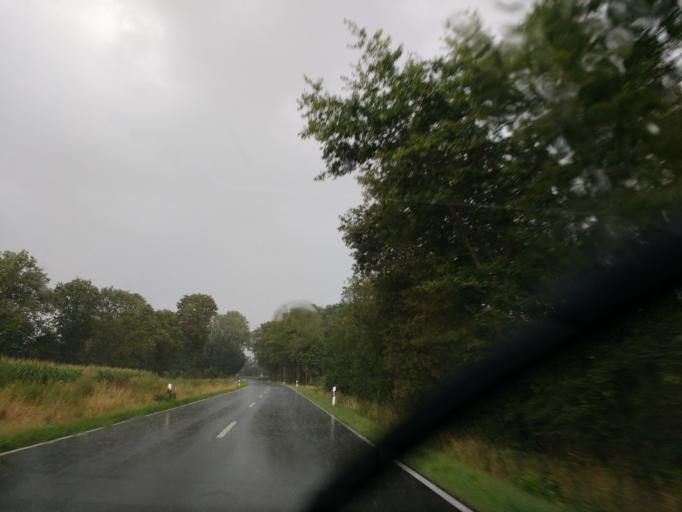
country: DE
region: North Rhine-Westphalia
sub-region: Regierungsbezirk Munster
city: Lienen
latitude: 52.1129
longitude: 7.9174
